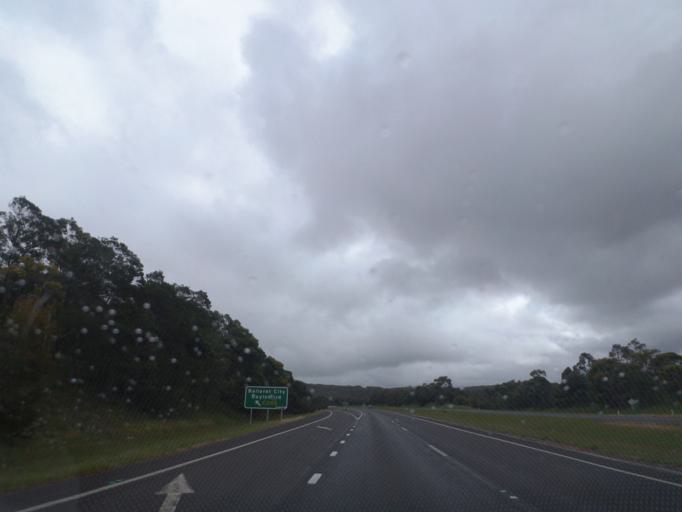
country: AU
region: Victoria
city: Brown Hill
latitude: -37.5534
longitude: 143.9108
